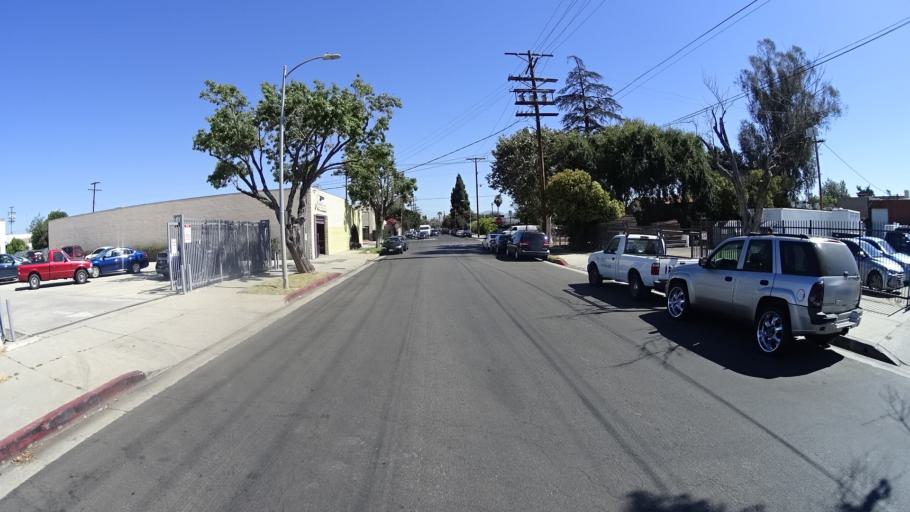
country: US
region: California
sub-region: Los Angeles County
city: Van Nuys
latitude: 34.1970
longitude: -118.4858
